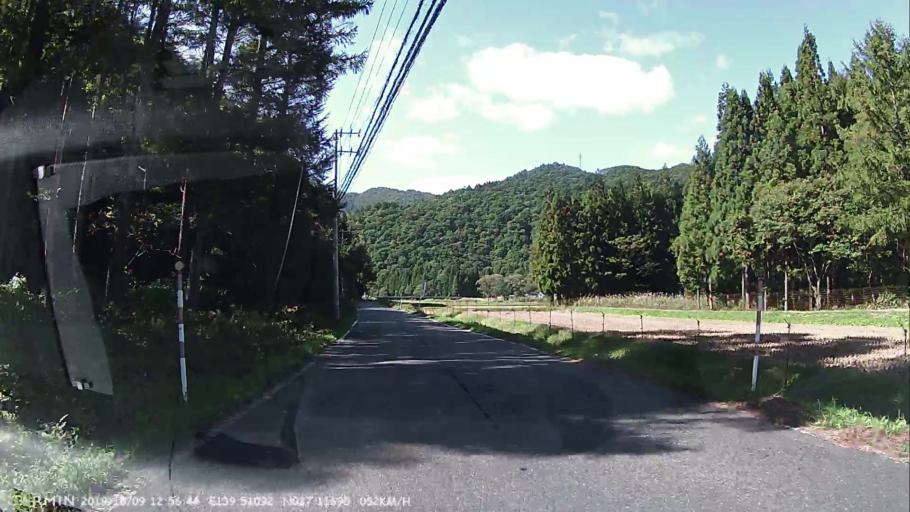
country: JP
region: Tochigi
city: Nikko
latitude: 37.1168
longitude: 139.5111
